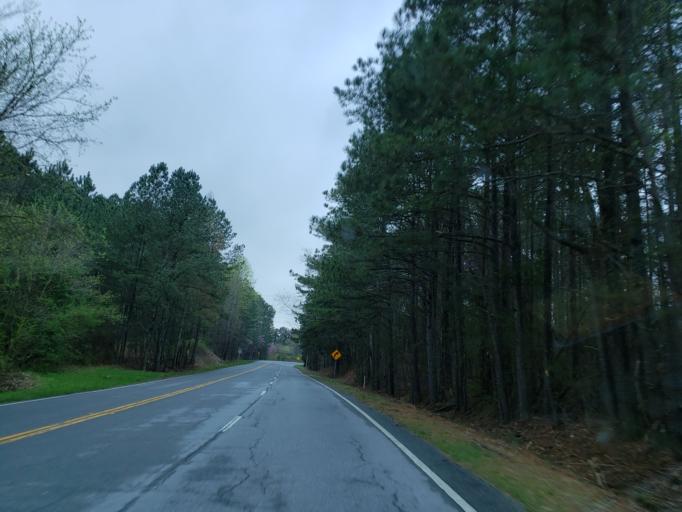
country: US
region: Georgia
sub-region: Polk County
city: Rockmart
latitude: 33.9231
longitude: -84.9727
